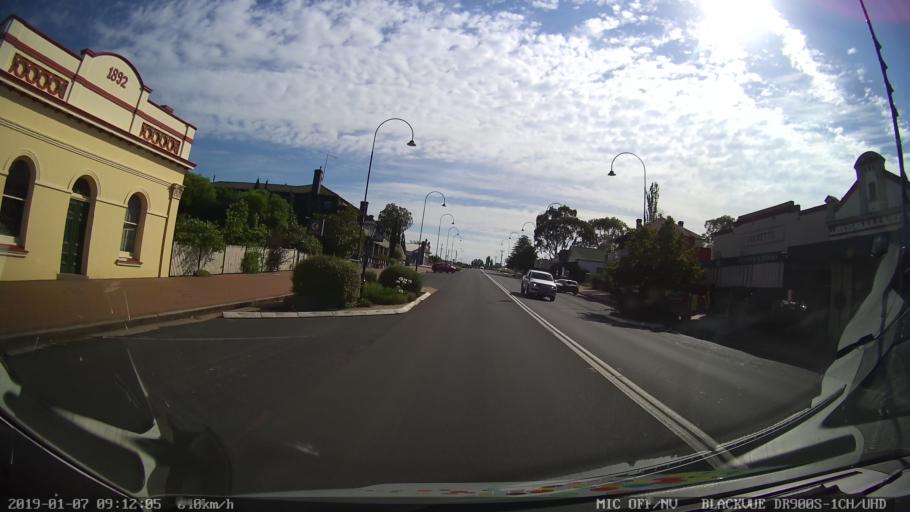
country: AU
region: New South Wales
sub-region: Armidale Dumaresq
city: Armidale
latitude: -30.6414
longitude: 151.5009
